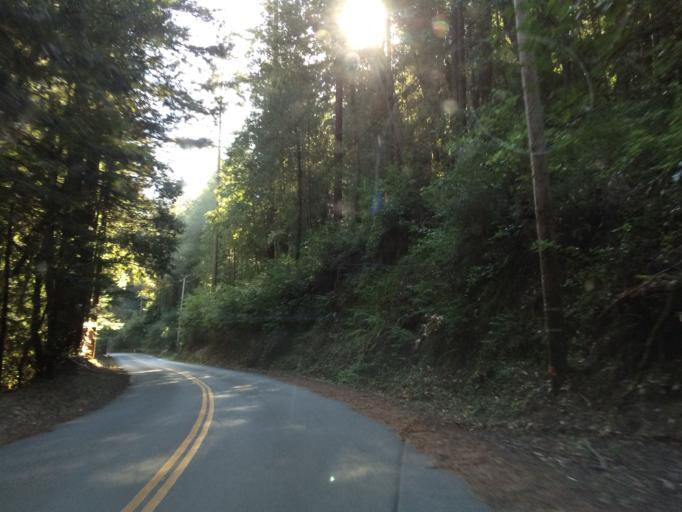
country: US
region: California
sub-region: Santa Cruz County
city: Boulder Creek
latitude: 37.1496
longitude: -122.1721
